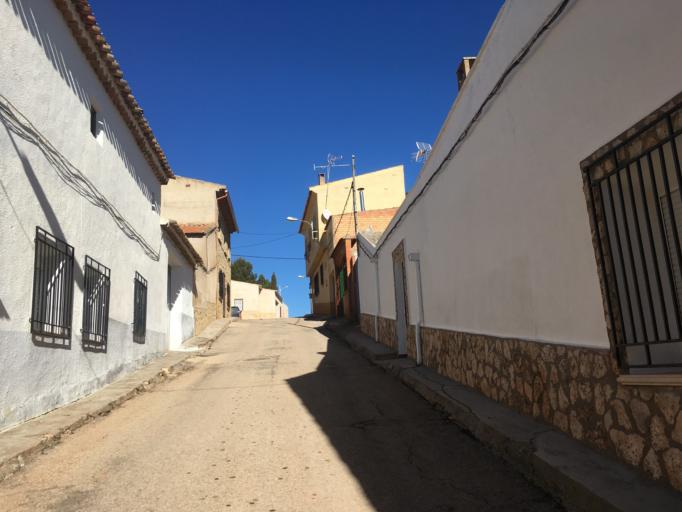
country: ES
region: Castille-La Mancha
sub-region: Provincia de Cuenca
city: Atalaya del Canavate
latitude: 39.5481
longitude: -2.2476
